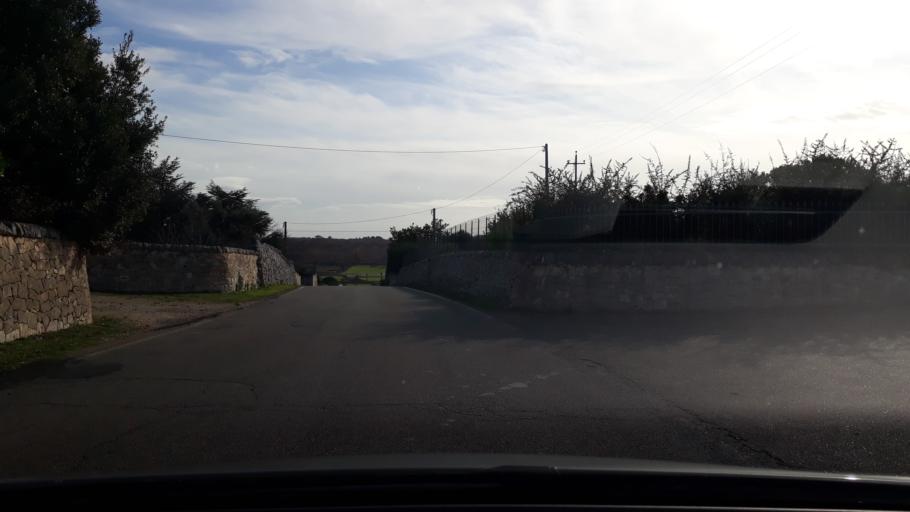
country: IT
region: Apulia
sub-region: Provincia di Taranto
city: Martina Franca
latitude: 40.6829
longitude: 17.3523
